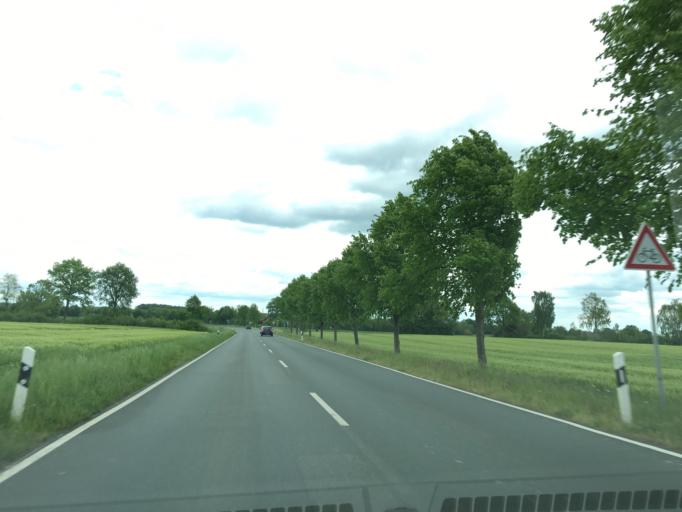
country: DE
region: North Rhine-Westphalia
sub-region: Regierungsbezirk Munster
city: Havixbeck
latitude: 51.9239
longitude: 7.4609
